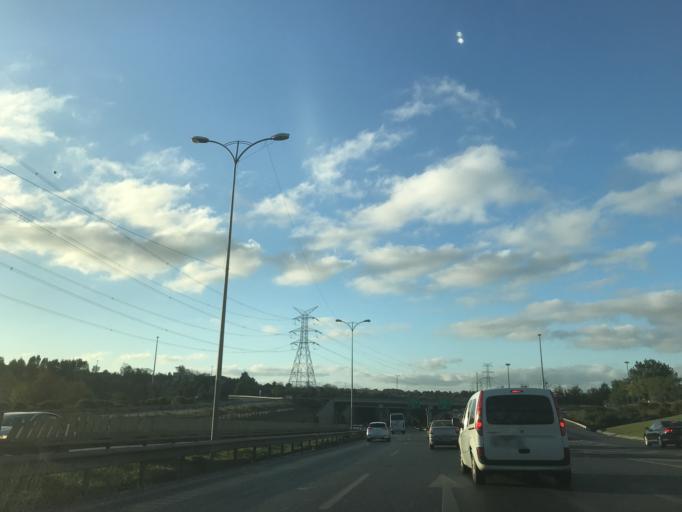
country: TR
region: Istanbul
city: Sultangazi
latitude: 41.0762
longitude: 28.8748
